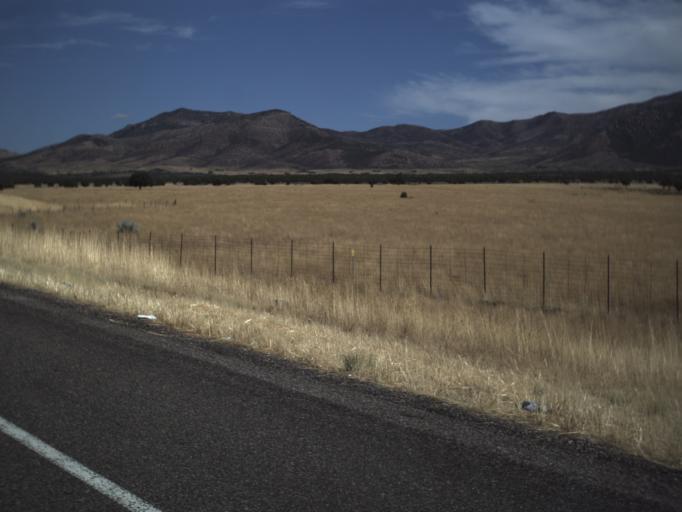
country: US
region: Utah
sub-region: Millard County
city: Fillmore
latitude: 39.1427
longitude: -112.2358
